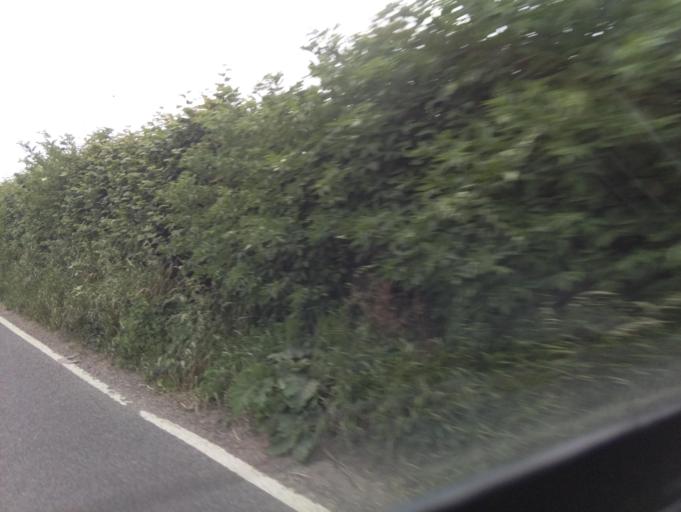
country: GB
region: England
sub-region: Dorset
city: Bridport
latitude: 50.7600
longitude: -2.7361
